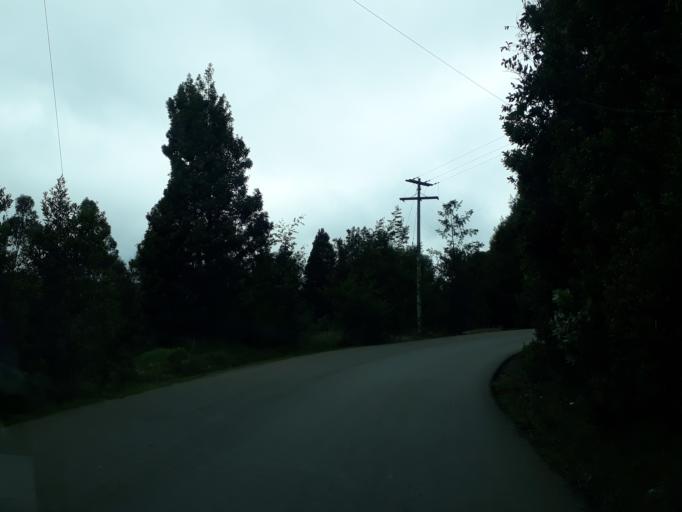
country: CO
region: Cundinamarca
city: Cucunuba
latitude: 5.1994
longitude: -73.7894
